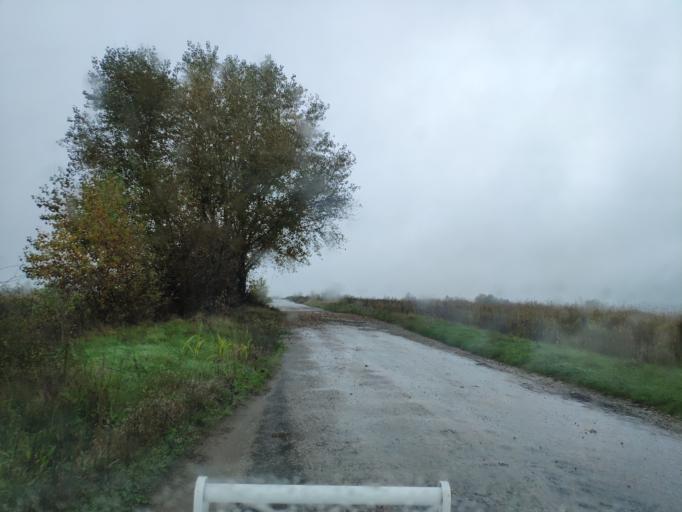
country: SK
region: Kosicky
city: Cierna nad Tisou
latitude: 48.4245
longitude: 21.9971
